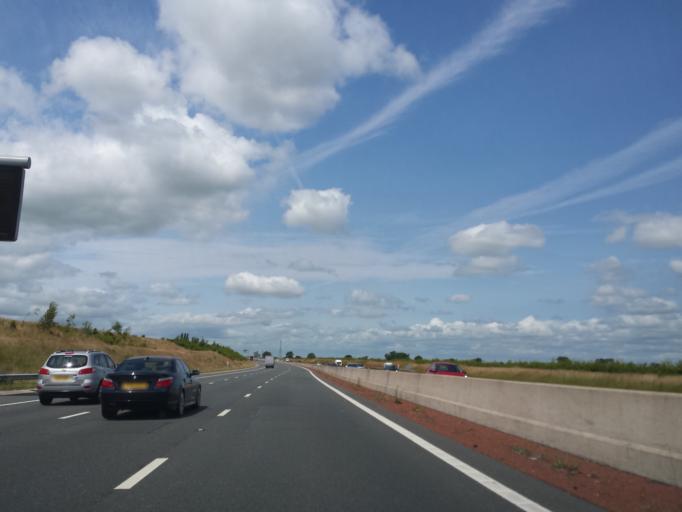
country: GB
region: England
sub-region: North Yorkshire
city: Ripon
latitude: 54.2151
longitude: -1.4805
